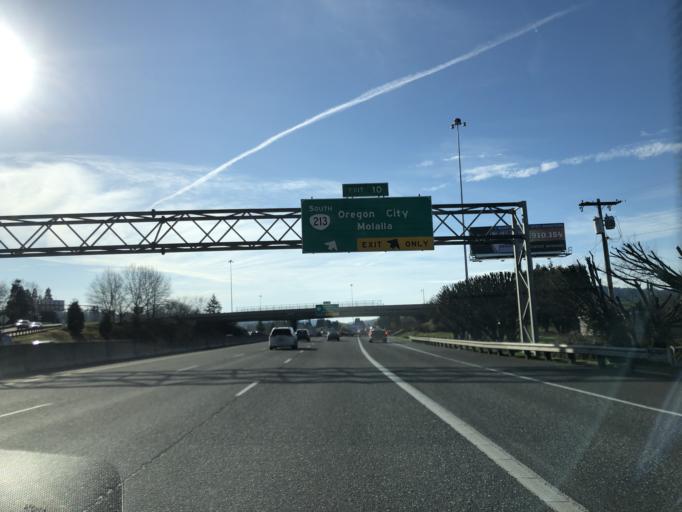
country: US
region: Oregon
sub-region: Clackamas County
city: Gladstone
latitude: 45.3762
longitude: -122.5855
